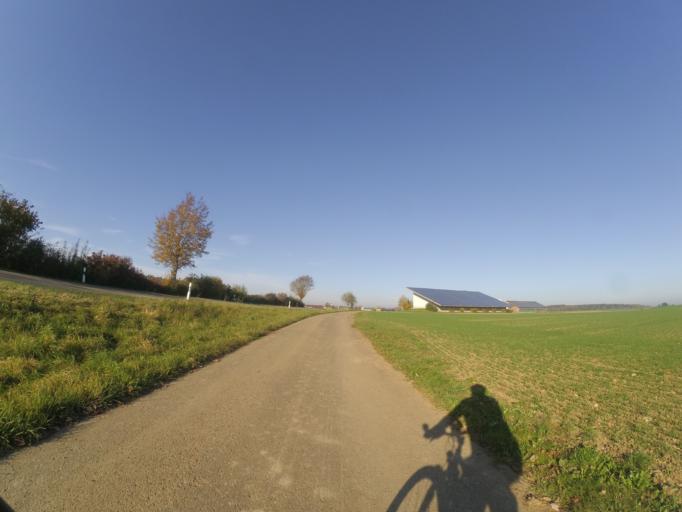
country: DE
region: Baden-Wuerttemberg
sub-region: Tuebingen Region
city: Blaubeuren
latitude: 48.4225
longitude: 9.8134
